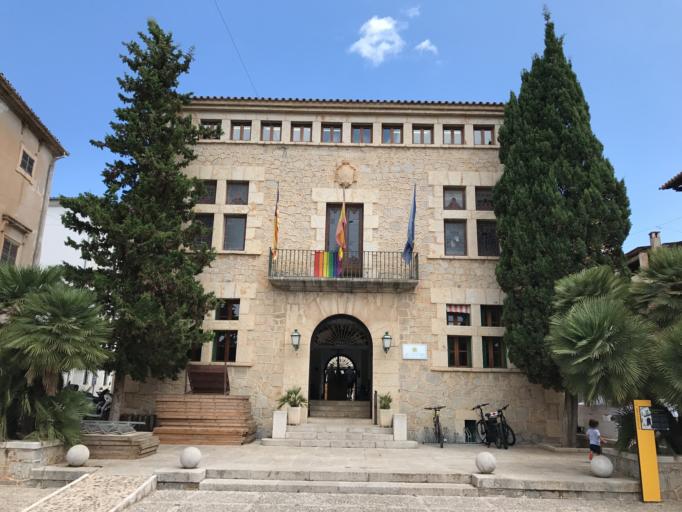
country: ES
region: Balearic Islands
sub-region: Illes Balears
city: Arta
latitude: 39.6949
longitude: 3.3511
